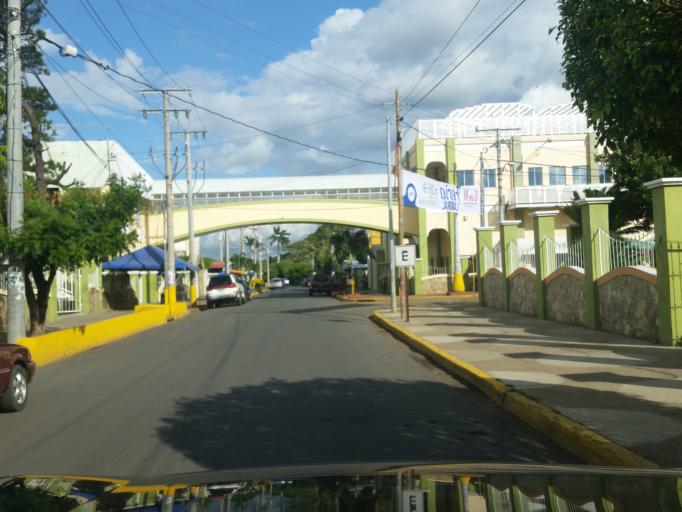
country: NI
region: Managua
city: Ciudad Sandino
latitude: 12.1267
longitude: -86.3100
